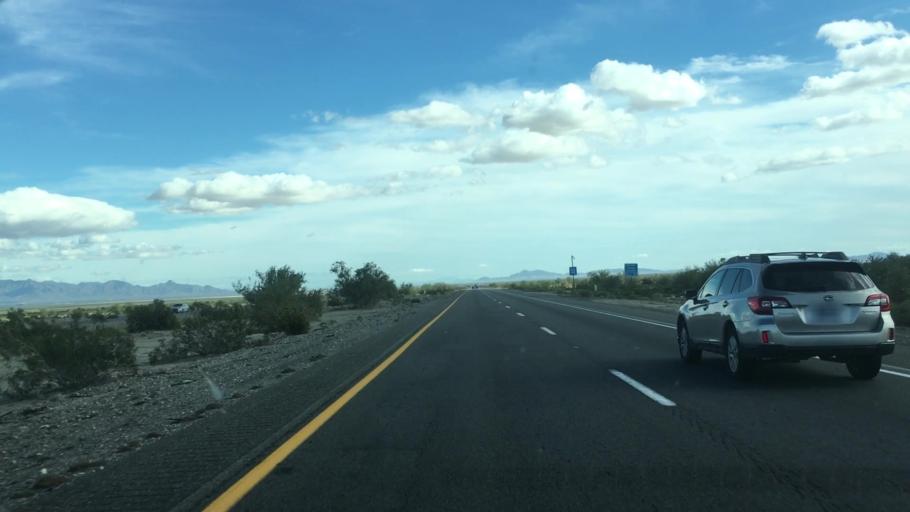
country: US
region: California
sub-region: Riverside County
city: Mesa Verde
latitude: 33.6555
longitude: -115.1527
